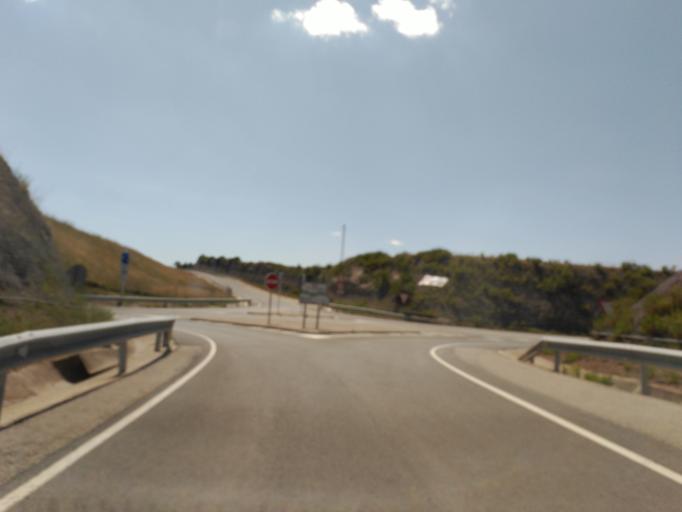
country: ES
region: Catalonia
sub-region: Provincia de Barcelona
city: Orista
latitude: 41.9027
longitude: 2.0914
